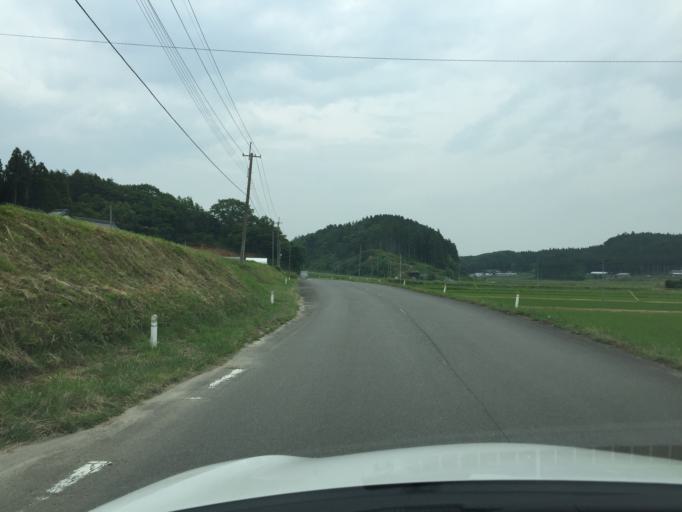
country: JP
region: Fukushima
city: Iwaki
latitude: 37.1884
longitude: 140.7186
